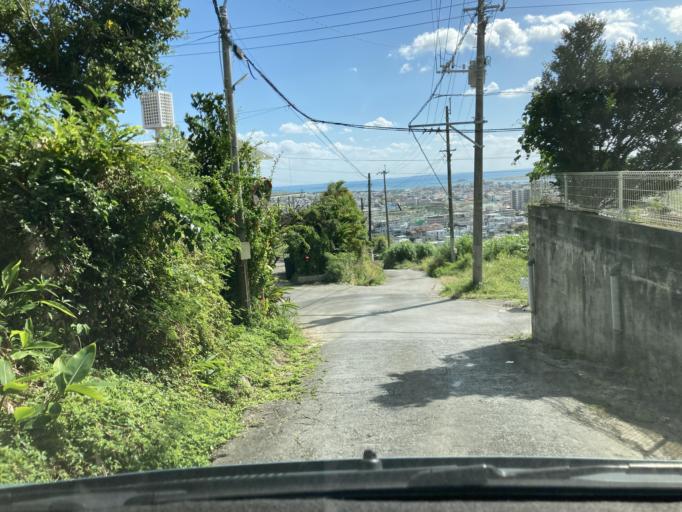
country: JP
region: Okinawa
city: Okinawa
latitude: 26.3273
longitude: 127.8174
